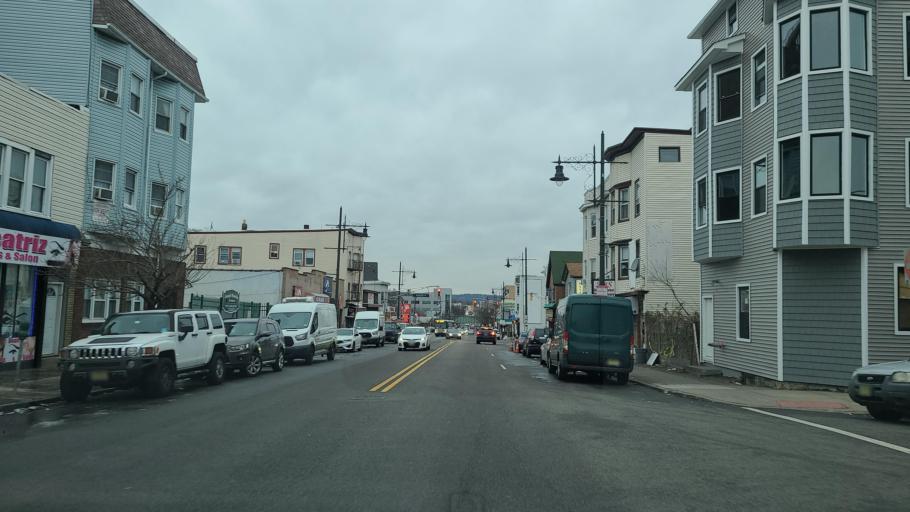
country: US
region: New Jersey
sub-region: Passaic County
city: Paterson
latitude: 40.8978
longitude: -74.1624
